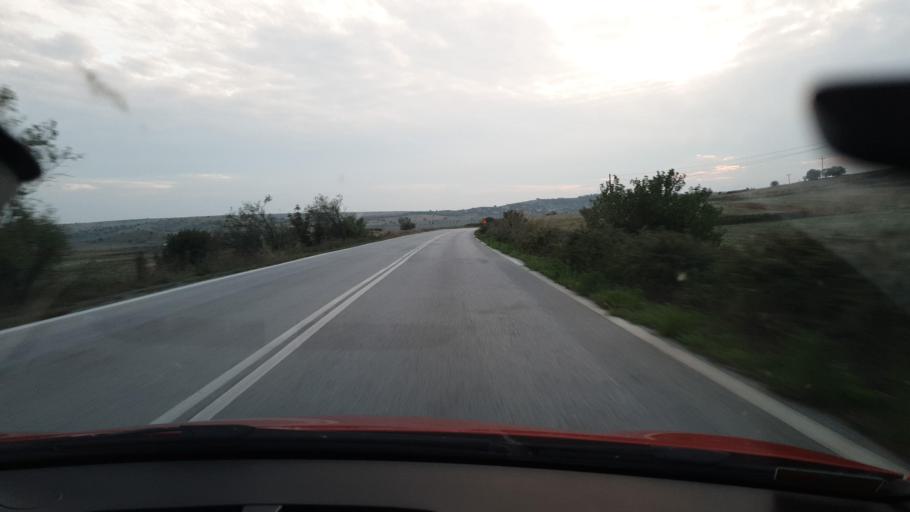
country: GR
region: Central Macedonia
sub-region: Nomos Kilkis
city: Kristoni
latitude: 40.9959
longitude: 22.7569
